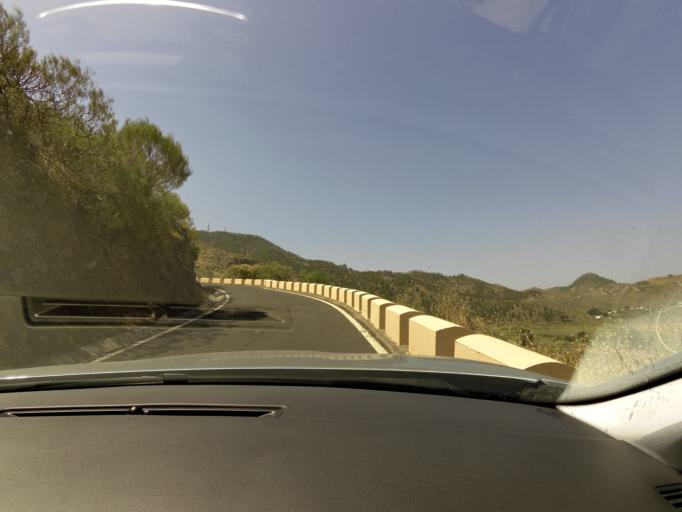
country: ES
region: Canary Islands
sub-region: Provincia de Santa Cruz de Tenerife
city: Santiago del Teide
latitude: 28.2982
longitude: -16.8200
